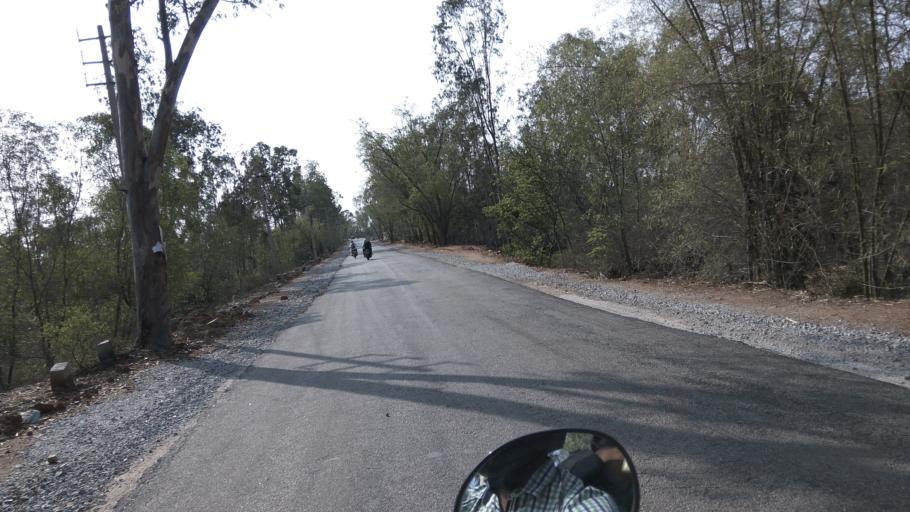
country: IN
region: Karnataka
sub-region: Kolar
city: Bangarapet
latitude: 13.0854
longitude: 78.2171
